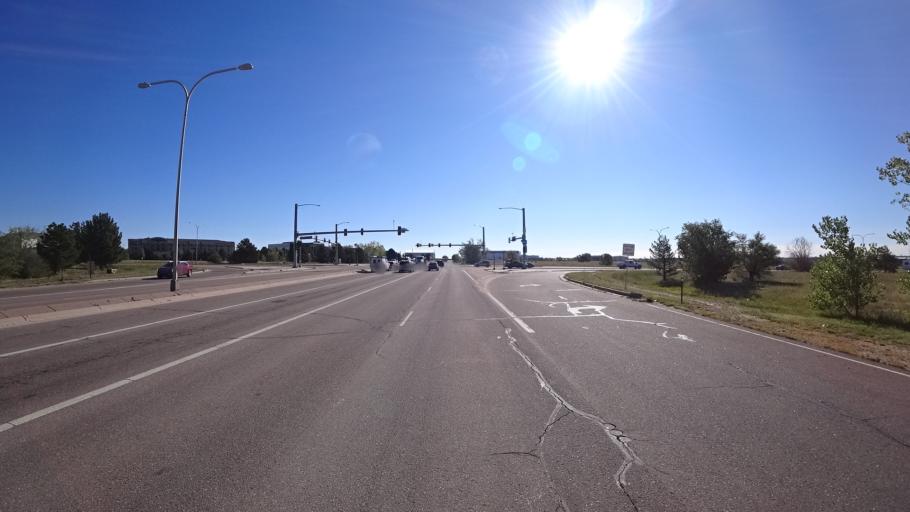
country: US
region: Colorado
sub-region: El Paso County
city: Stratmoor
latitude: 38.8061
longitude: -104.7313
